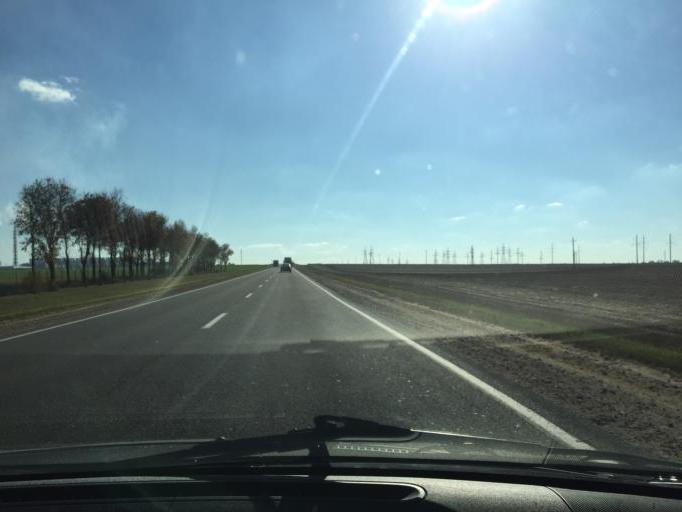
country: BY
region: Minsk
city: Salihorsk
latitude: 52.8677
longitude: 27.4671
